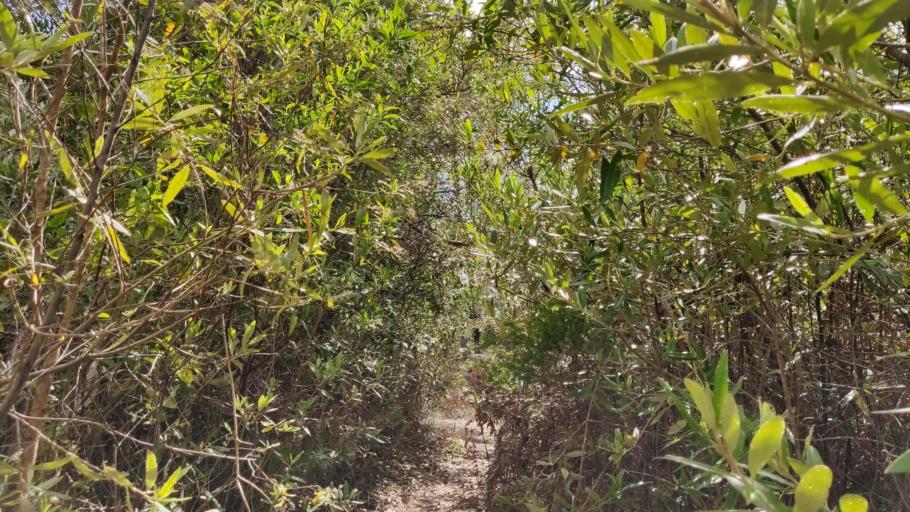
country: AU
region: New South Wales
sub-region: Port Macquarie-Hastings
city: North Haven
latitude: -31.6435
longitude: 152.8362
